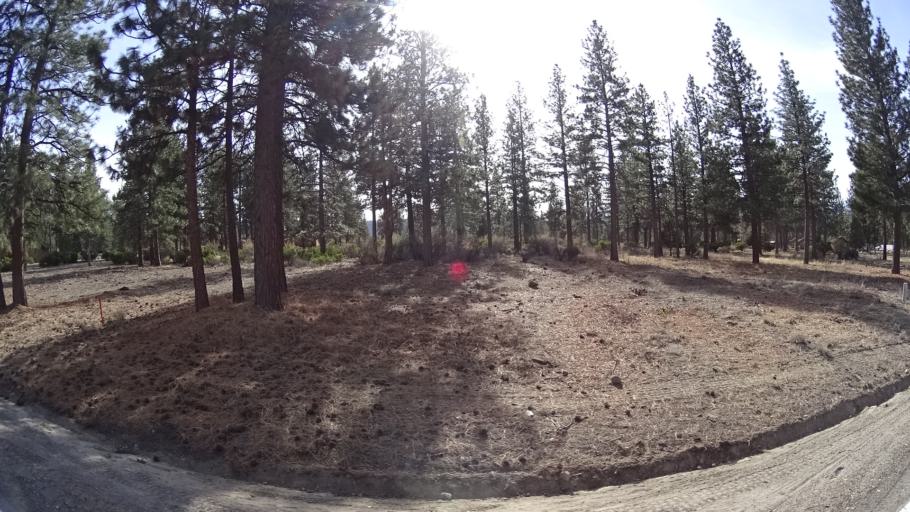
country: US
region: California
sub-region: Siskiyou County
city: Weed
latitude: 41.4940
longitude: -122.3716
